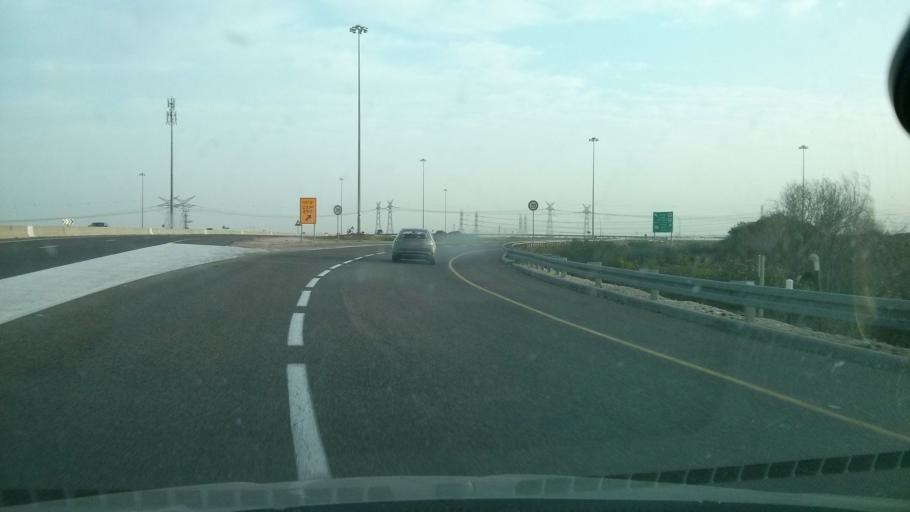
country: IL
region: Haifa
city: Hadera
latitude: 32.4696
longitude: 34.8983
